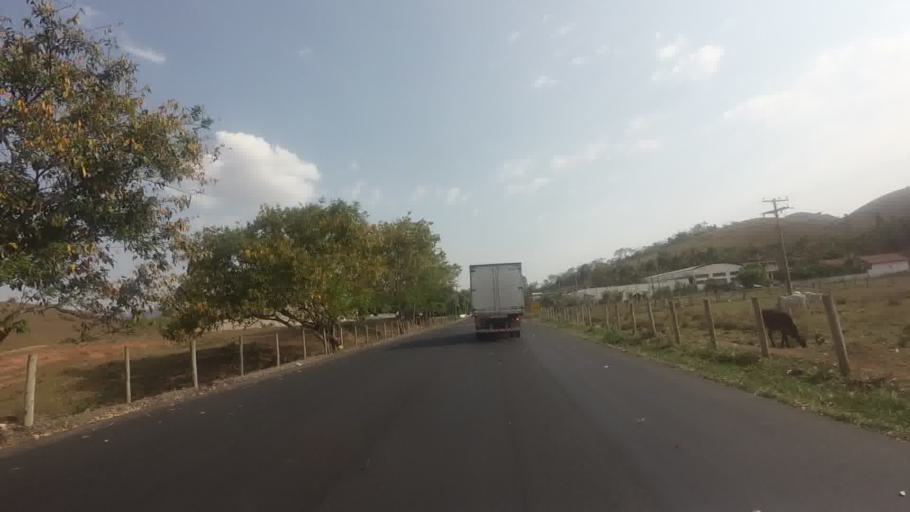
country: BR
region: Rio de Janeiro
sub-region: Bom Jesus Do Itabapoana
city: Bom Jesus do Itabapoana
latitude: -21.1520
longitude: -41.6683
